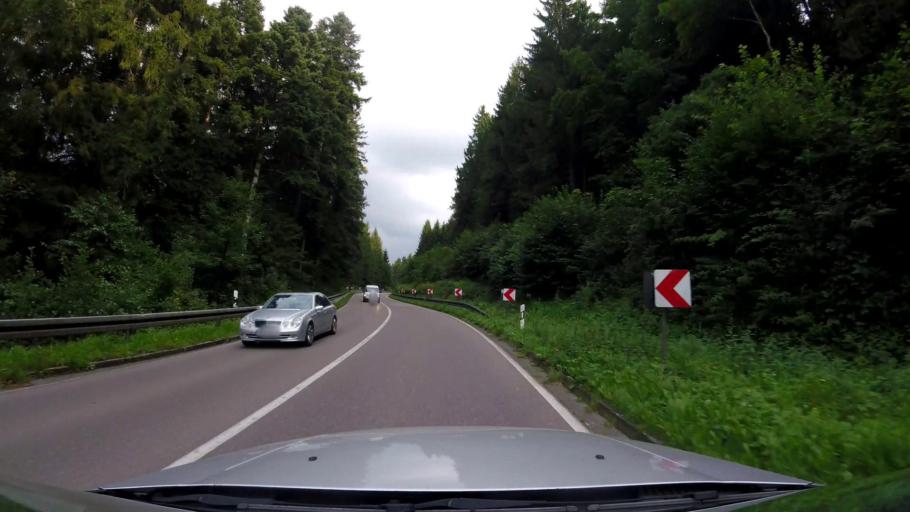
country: DE
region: Baden-Wuerttemberg
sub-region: Regierungsbezirk Stuttgart
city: Durlangen
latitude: 48.8478
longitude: 9.7765
